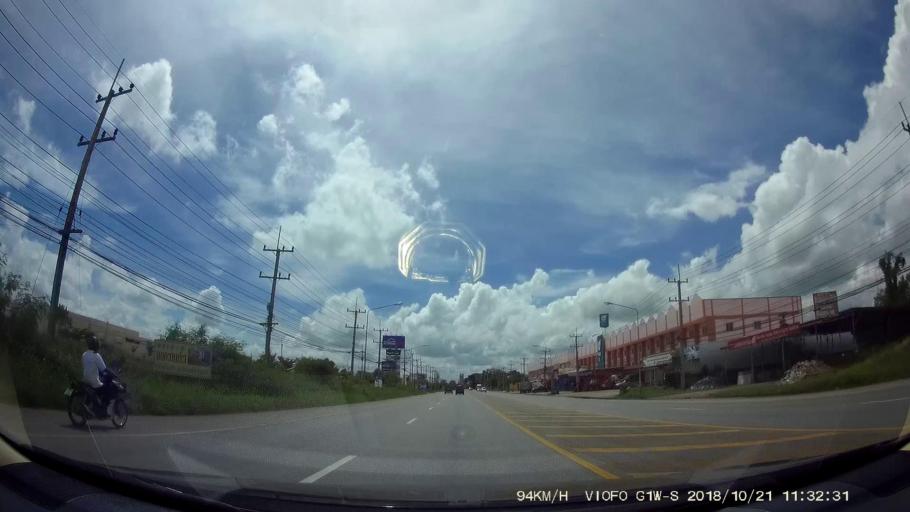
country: TH
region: Chaiyaphum
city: Chaiyaphum
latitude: 15.7574
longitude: 102.0243
